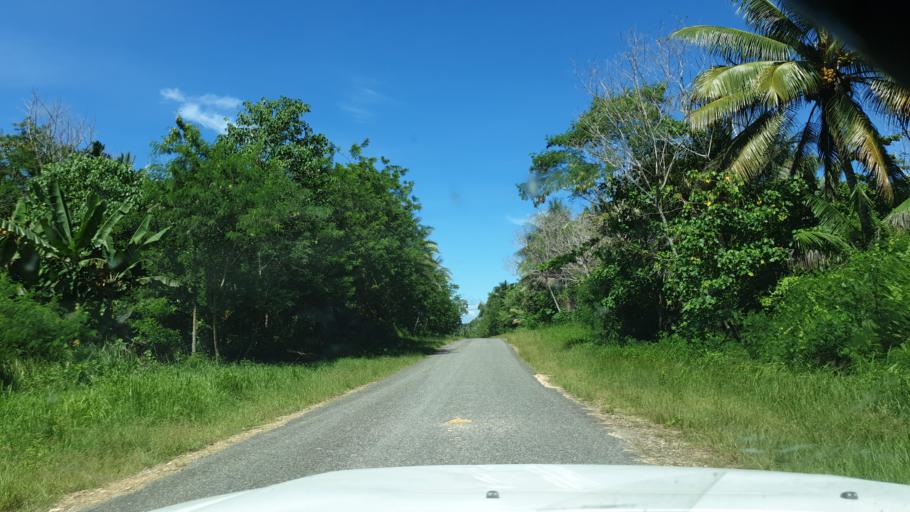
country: PG
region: Madang
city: Madang
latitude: -4.4499
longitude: 145.3688
